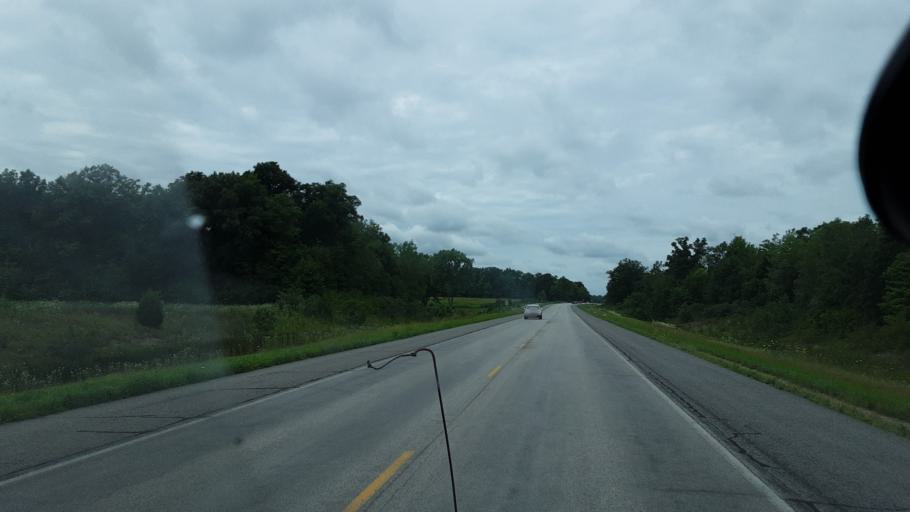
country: US
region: Indiana
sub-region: Adams County
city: Decatur
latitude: 40.8030
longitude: -84.9249
